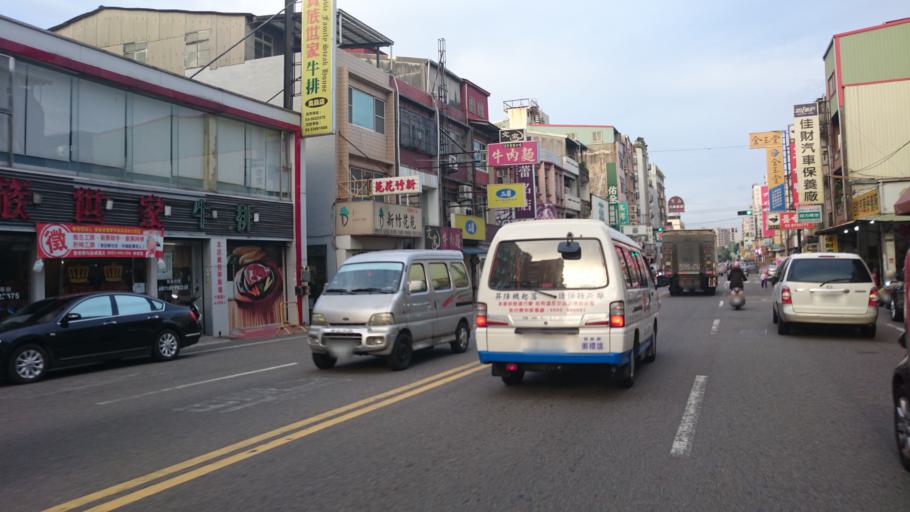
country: TW
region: Taiwan
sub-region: Hsinchu
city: Hsinchu
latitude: 24.7968
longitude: 120.9758
